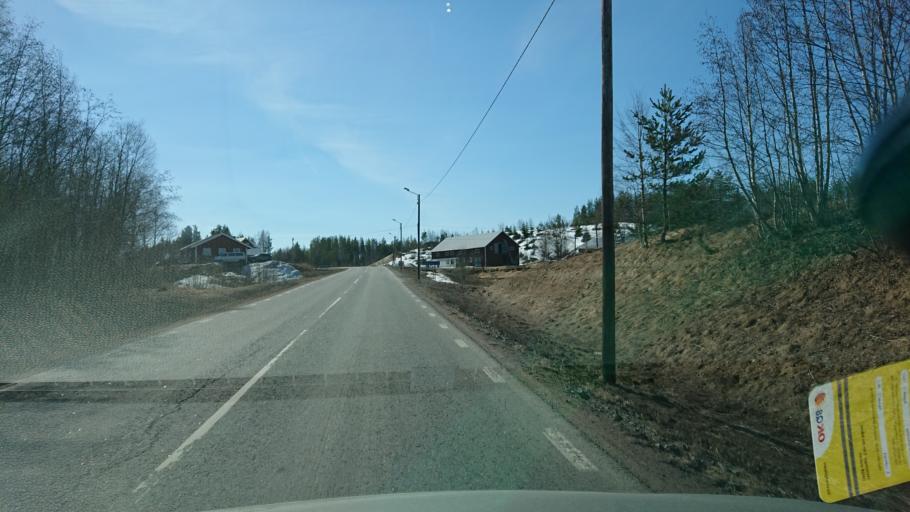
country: SE
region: Vaesternorrland
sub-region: Solleftea Kommun
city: As
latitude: 63.6463
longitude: 16.4574
